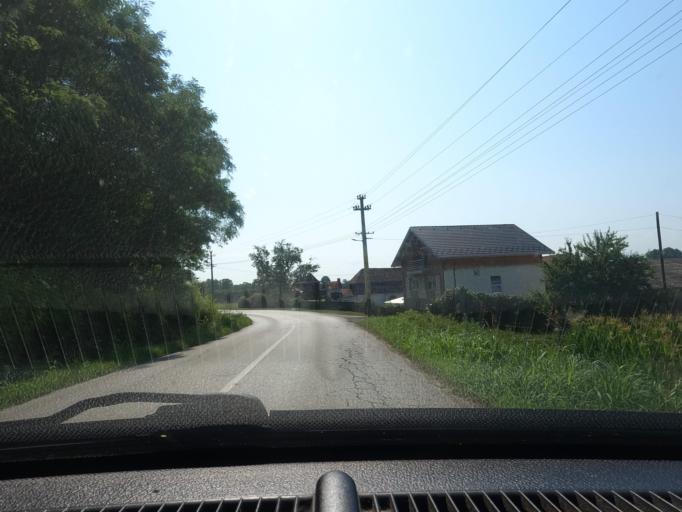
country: RS
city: Jadranska Lesnica
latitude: 44.5483
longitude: 19.3437
